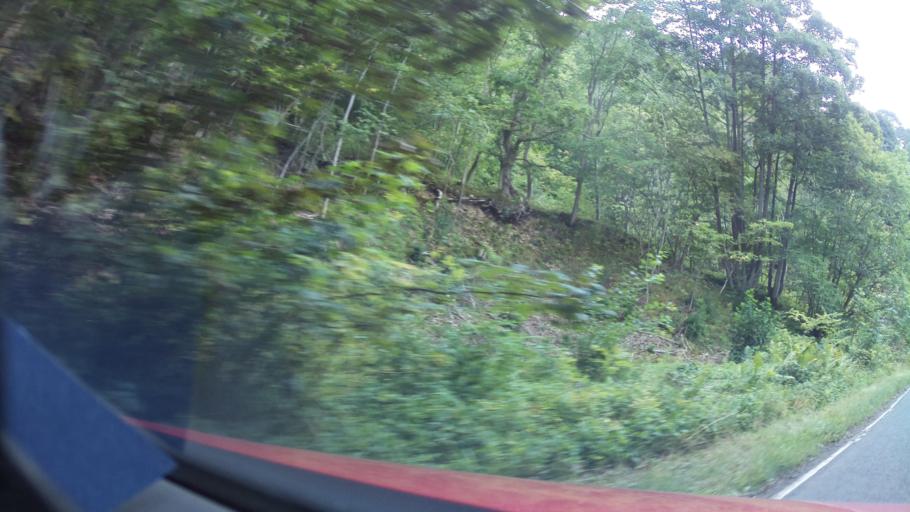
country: GB
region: England
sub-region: North Yorkshire
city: Leyburn
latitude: 54.3894
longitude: -1.8267
